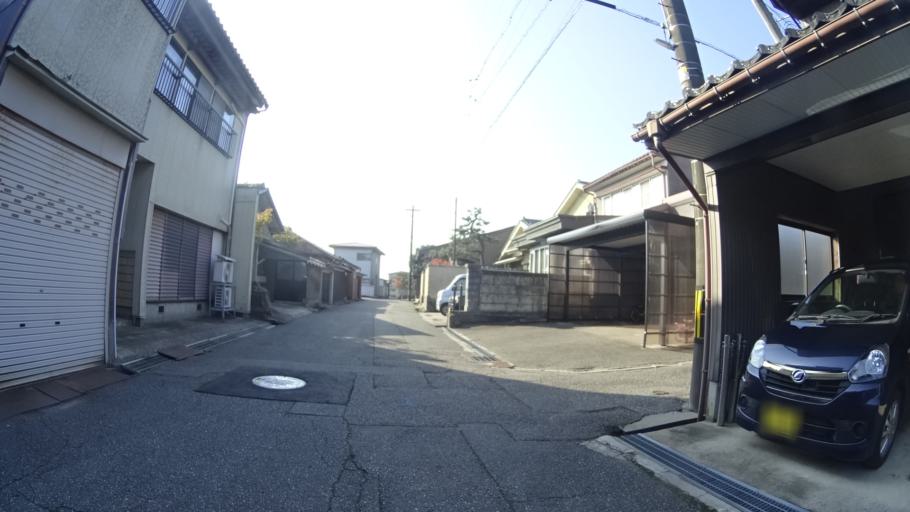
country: JP
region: Toyama
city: Nishishinminato
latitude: 36.7936
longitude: 137.0574
